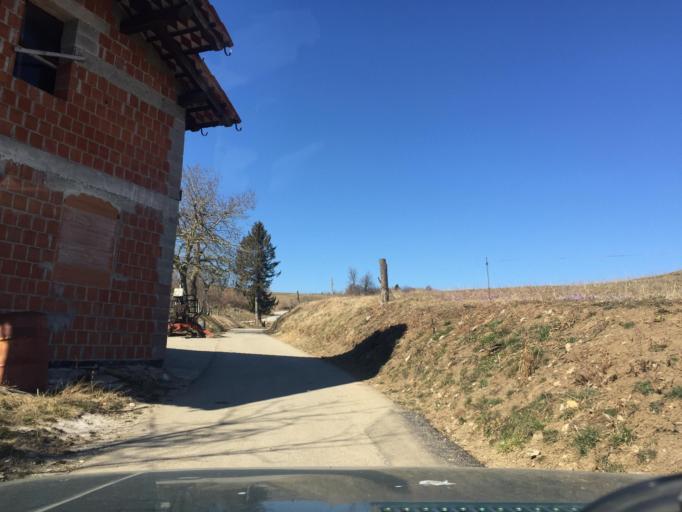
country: SI
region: Kanal
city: Kanal
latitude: 46.0787
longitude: 13.6623
